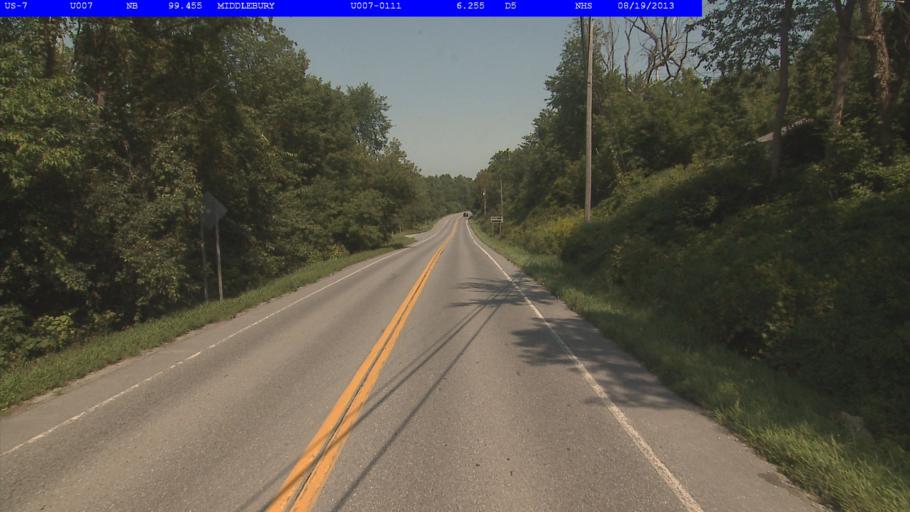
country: US
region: Vermont
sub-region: Addison County
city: Middlebury (village)
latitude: 44.0306
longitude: -73.1669
